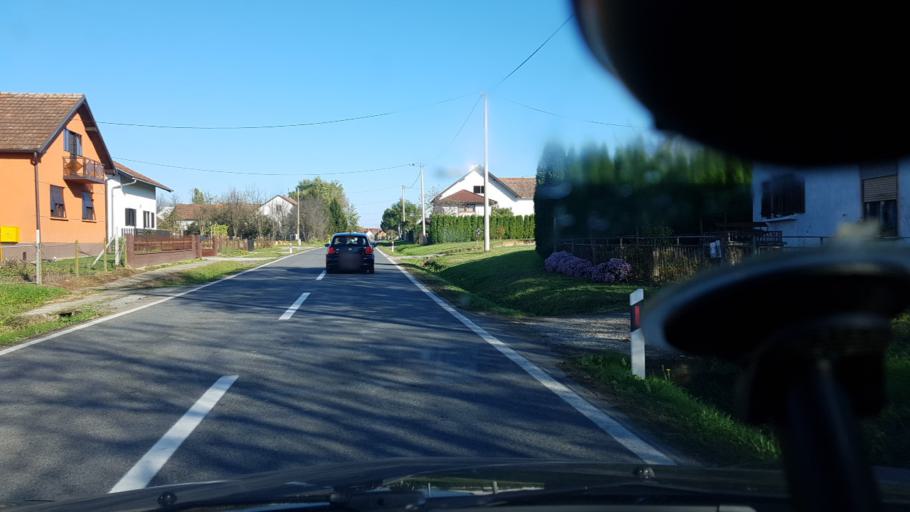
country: HR
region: Bjelovarsko-Bilogorska
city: Gudovac
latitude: 45.8330
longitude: 16.8015
